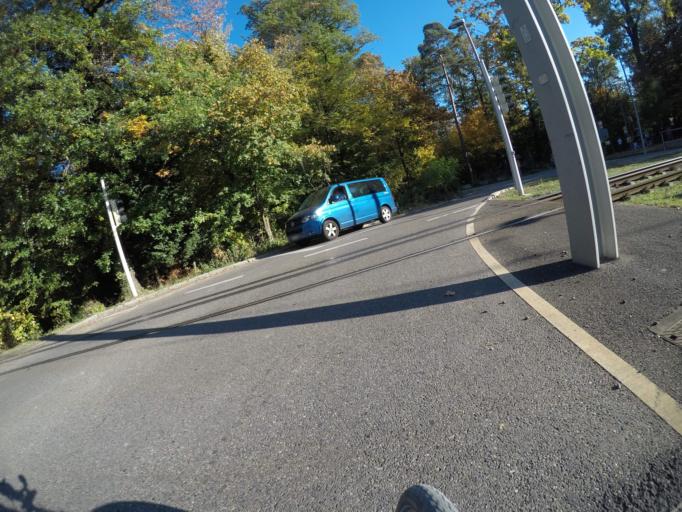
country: DE
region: Baden-Wuerttemberg
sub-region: Regierungsbezirk Stuttgart
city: Stuttgart-Ost
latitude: 48.7616
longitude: 9.2003
